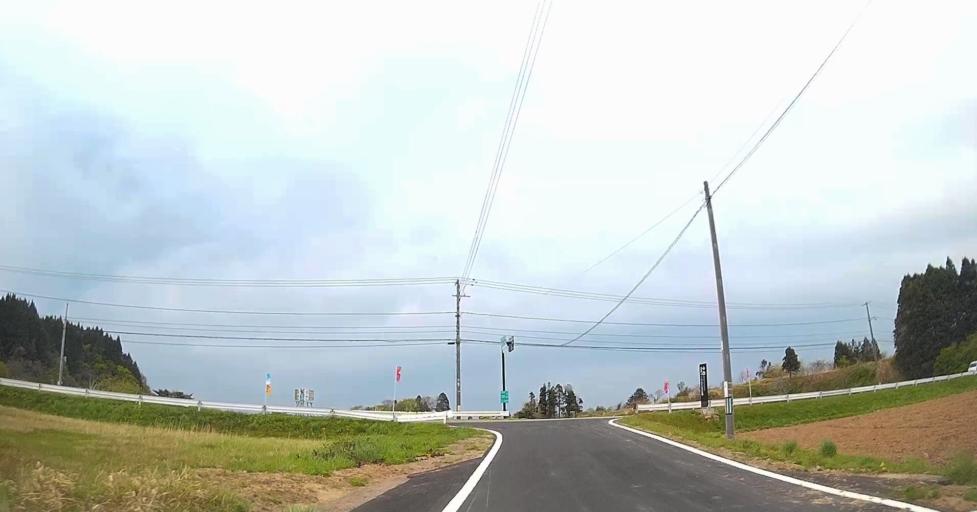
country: JP
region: Aomori
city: Shimokizukuri
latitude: 41.1803
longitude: 140.4602
